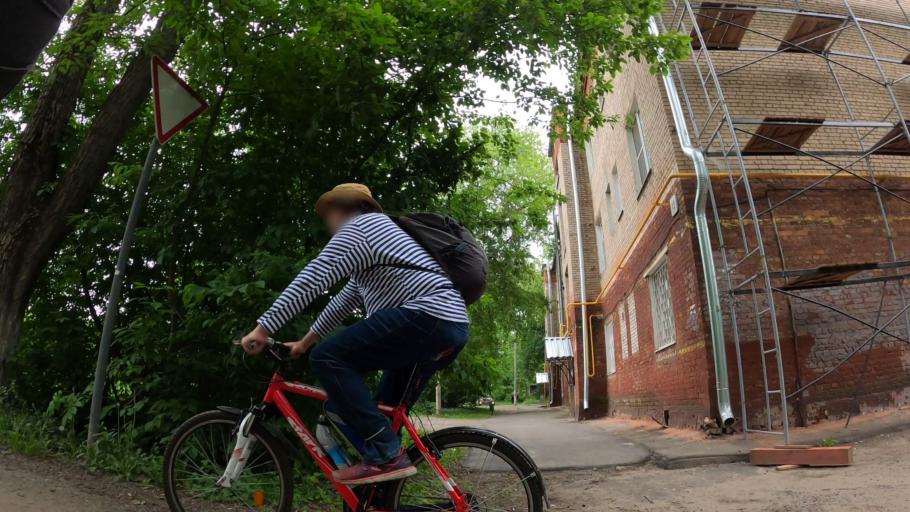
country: RU
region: Moskovskaya
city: Lesnyye Polyany
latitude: 55.9453
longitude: 37.8631
